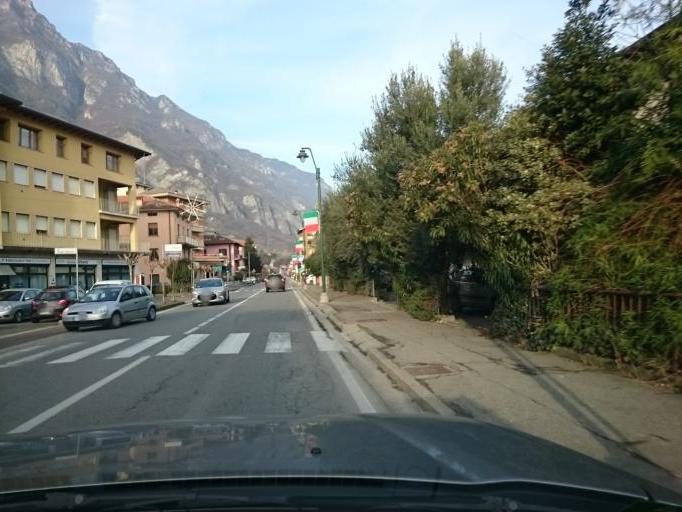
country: IT
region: Lombardy
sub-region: Provincia di Brescia
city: Darfo Boario Terme
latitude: 45.8953
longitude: 10.1903
